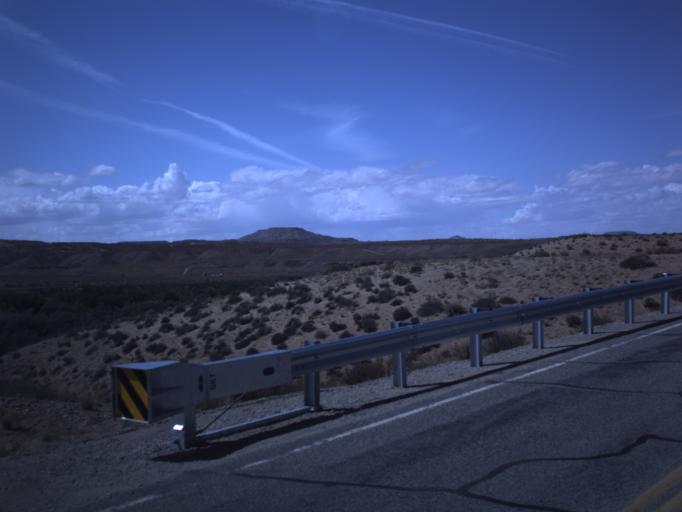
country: US
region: Utah
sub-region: San Juan County
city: Blanding
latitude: 37.2380
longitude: -109.2326
